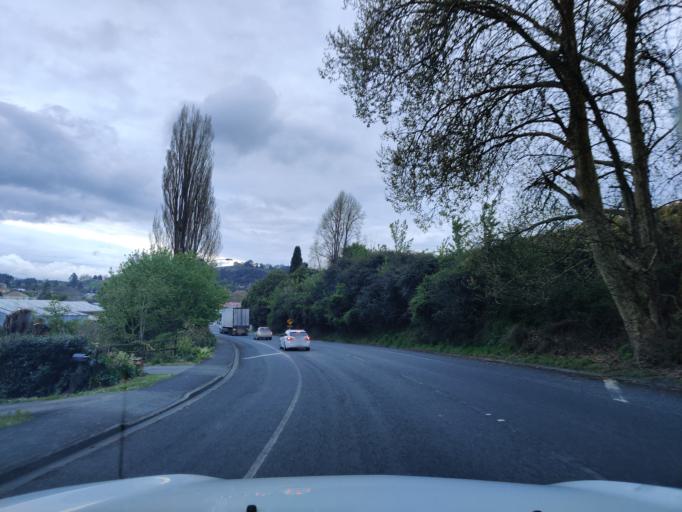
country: NZ
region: Waikato
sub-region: Otorohanga District
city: Otorohanga
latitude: -38.3403
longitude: 175.1672
